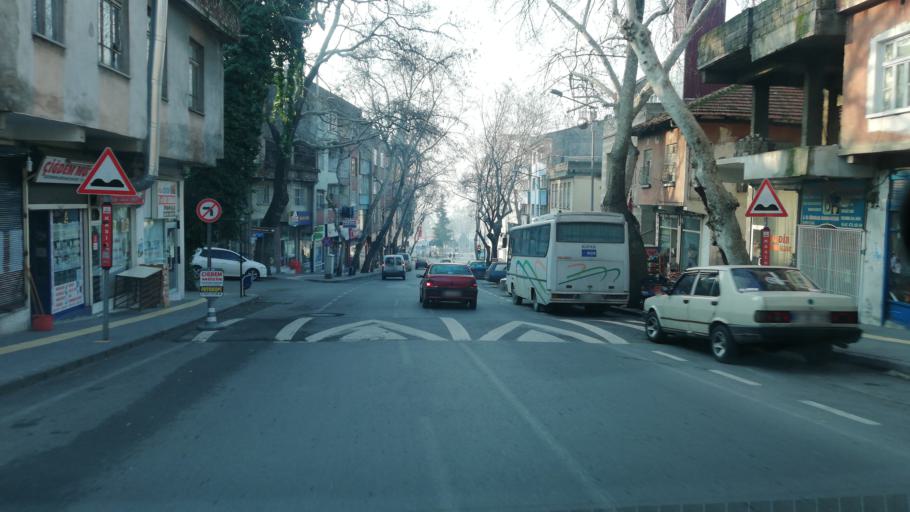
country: TR
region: Kahramanmaras
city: Kahramanmaras
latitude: 37.5880
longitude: 36.9271
